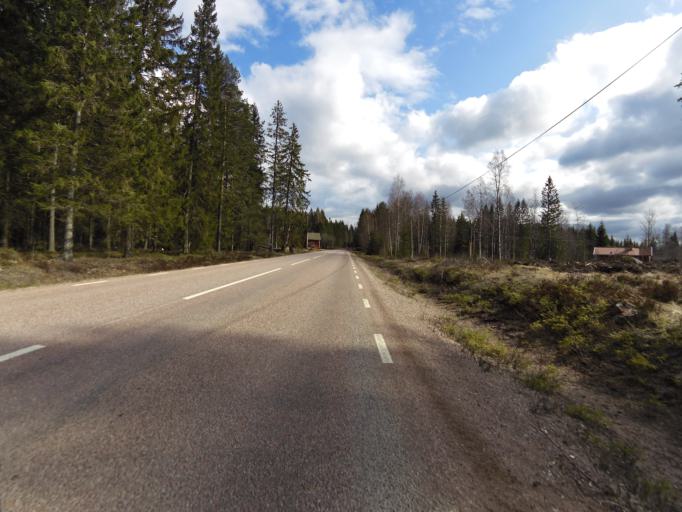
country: SE
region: Dalarna
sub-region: Avesta Kommun
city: Horndal
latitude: 60.3077
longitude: 16.2418
